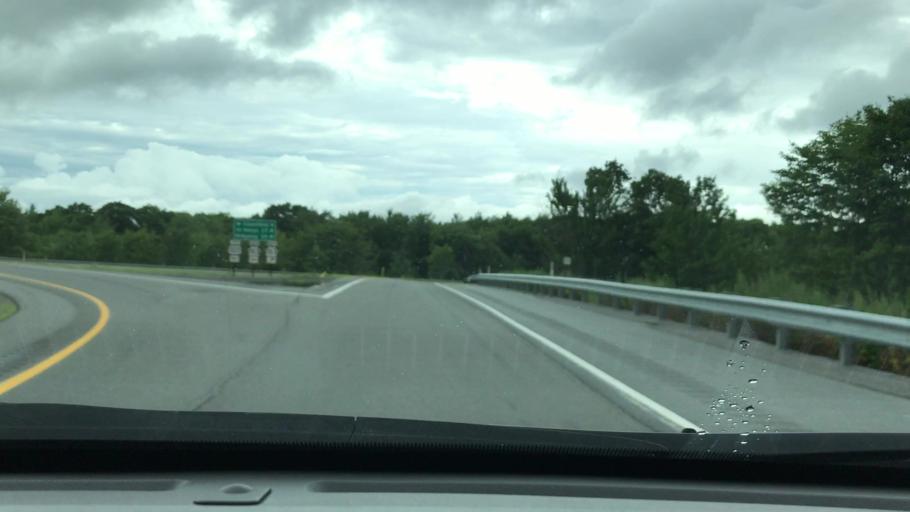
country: US
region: Pennsylvania
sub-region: Clearfield County
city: Clearfield
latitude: 41.1109
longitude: -78.5356
